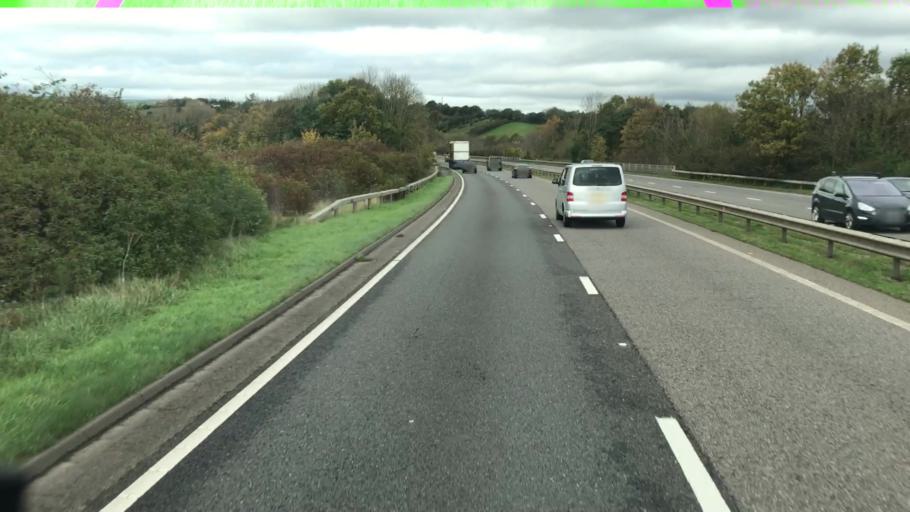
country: GB
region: England
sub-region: Devon
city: Exeter
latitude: 50.6999
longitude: -3.5434
